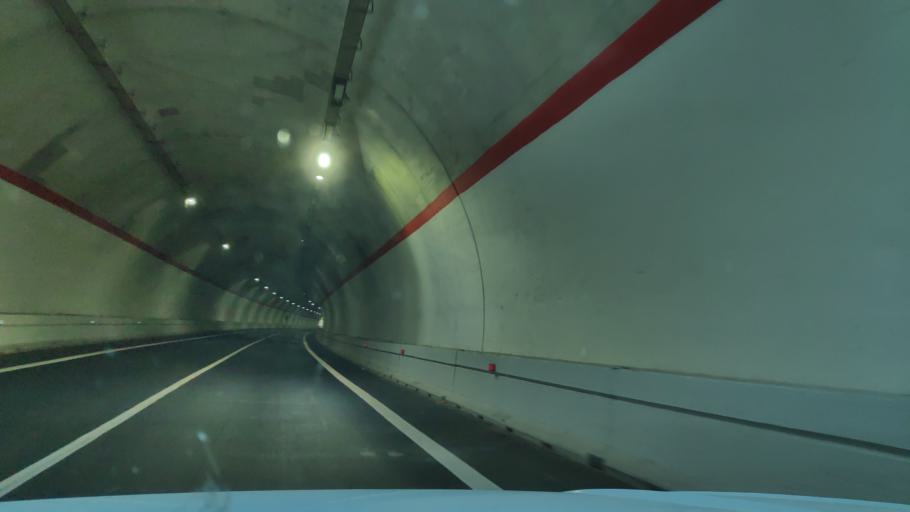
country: IT
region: Calabria
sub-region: Provincia di Reggio Calabria
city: Palizzi Marina
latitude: 37.9208
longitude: 15.9721
